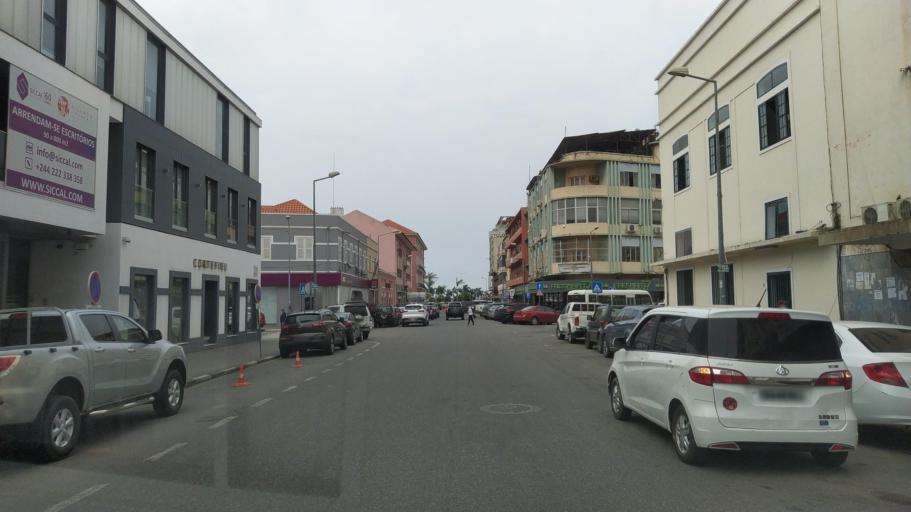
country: AO
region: Luanda
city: Luanda
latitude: -8.8121
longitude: 13.2349
